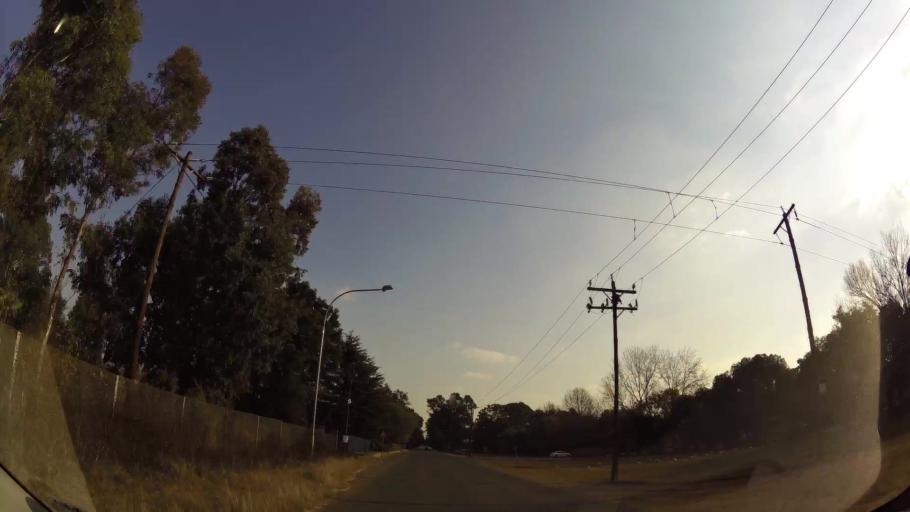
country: ZA
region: Gauteng
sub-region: Ekurhuleni Metropolitan Municipality
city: Benoni
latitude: -26.1077
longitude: 28.3733
